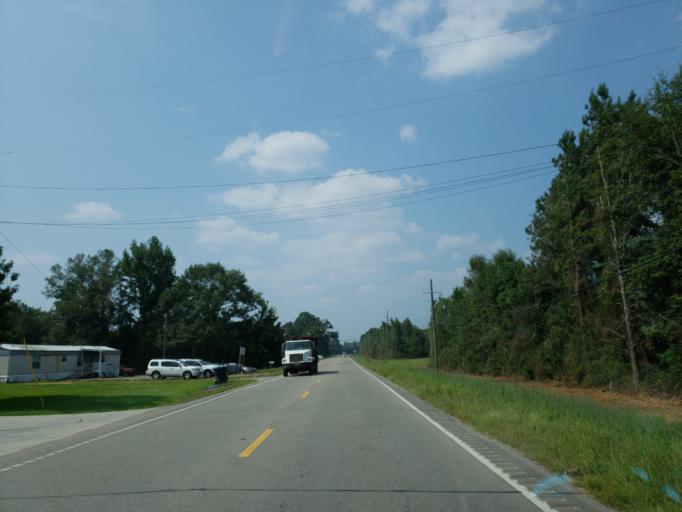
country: US
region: Mississippi
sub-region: Forrest County
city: Glendale
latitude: 31.4353
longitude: -89.2842
